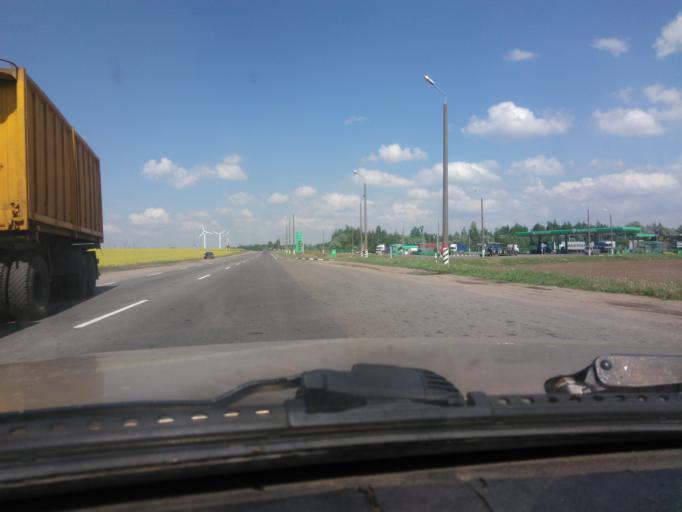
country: BY
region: Mogilev
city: Palykavichy Pyershyya
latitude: 53.9683
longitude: 30.3496
